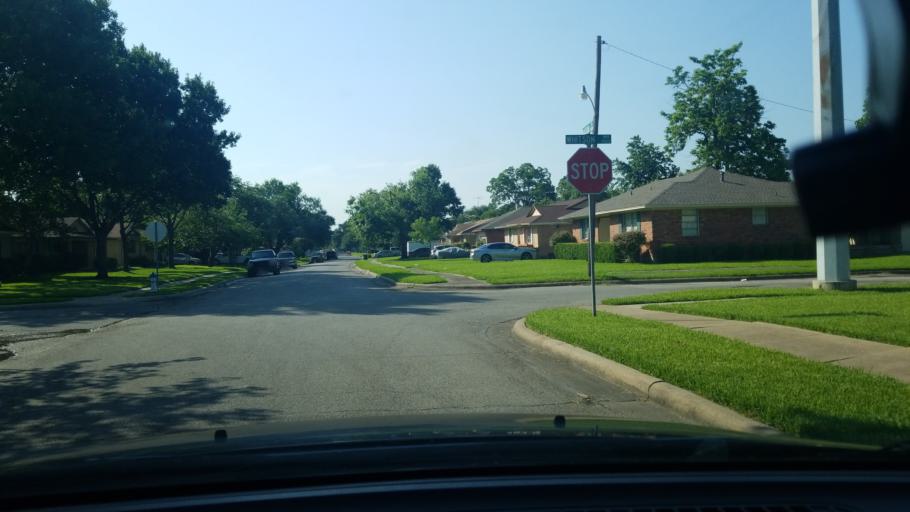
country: US
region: Texas
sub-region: Dallas County
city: Mesquite
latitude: 32.8243
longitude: -96.6423
